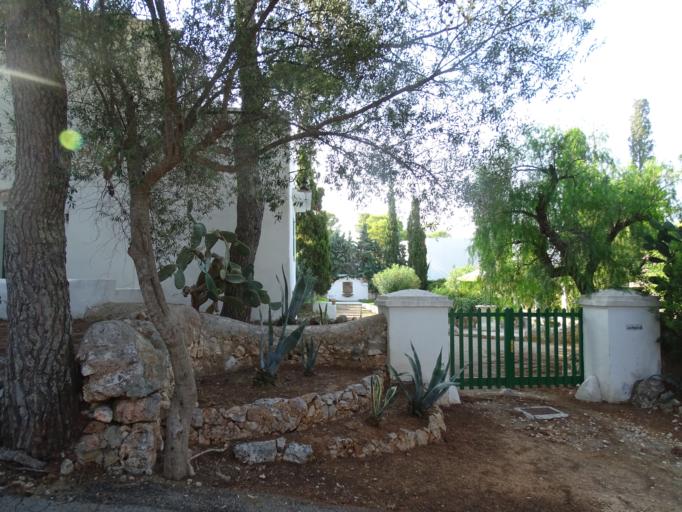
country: ES
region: Balearic Islands
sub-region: Illes Balears
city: Santanyi
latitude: 39.3715
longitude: 3.2307
